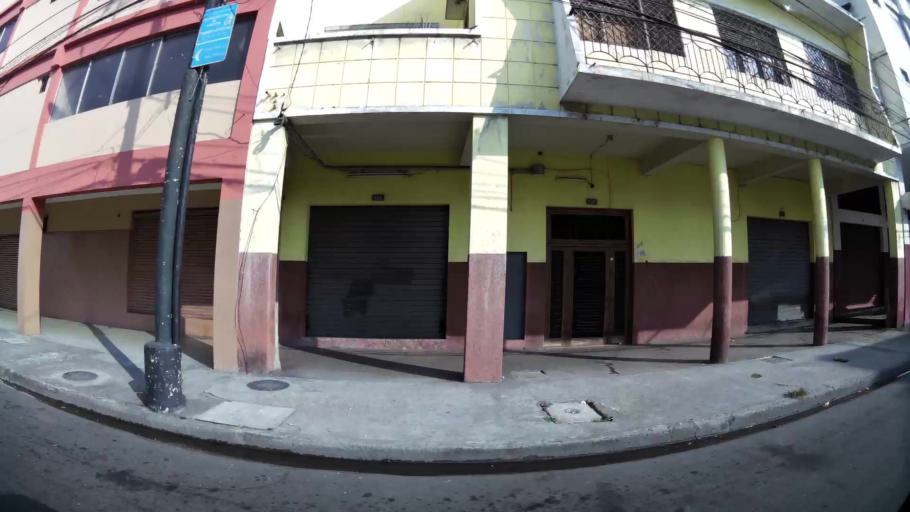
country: EC
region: Guayas
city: Eloy Alfaro
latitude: -2.1875
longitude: -79.8816
